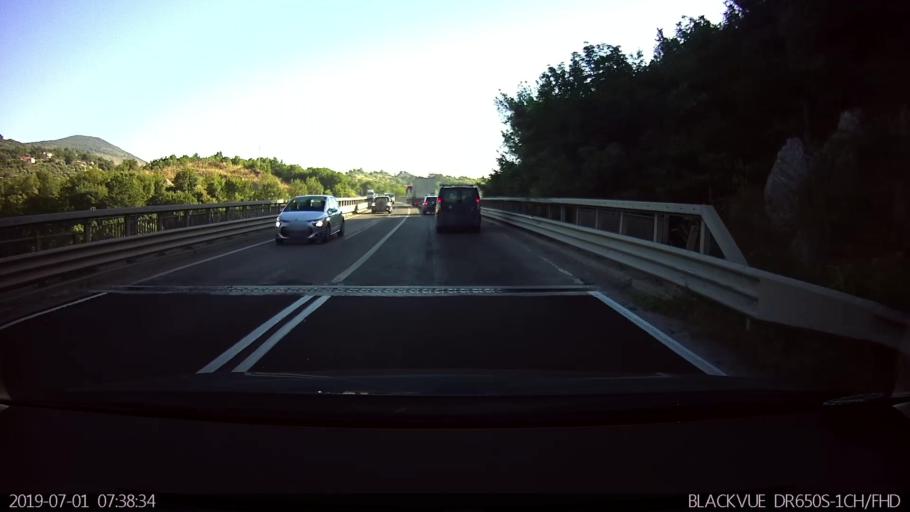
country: IT
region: Latium
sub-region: Provincia di Frosinone
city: Giuliano di Roma
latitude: 41.5441
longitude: 13.2690
